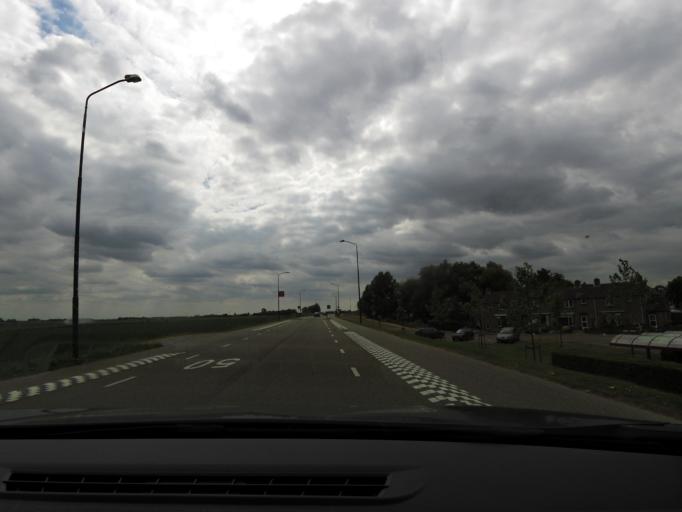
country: NL
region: North Brabant
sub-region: Gemeente Moerdijk
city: Klundert
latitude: 51.6605
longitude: 4.5301
